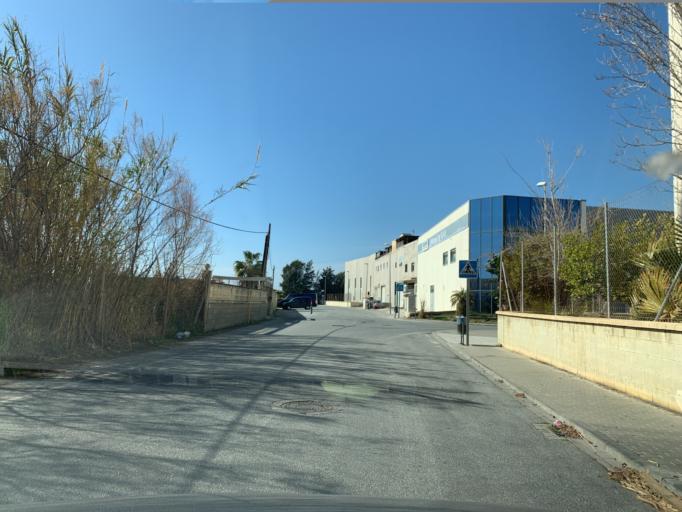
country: ES
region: Andalusia
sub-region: Provincia de Granada
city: El Varadero
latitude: 36.7270
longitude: -3.5453
